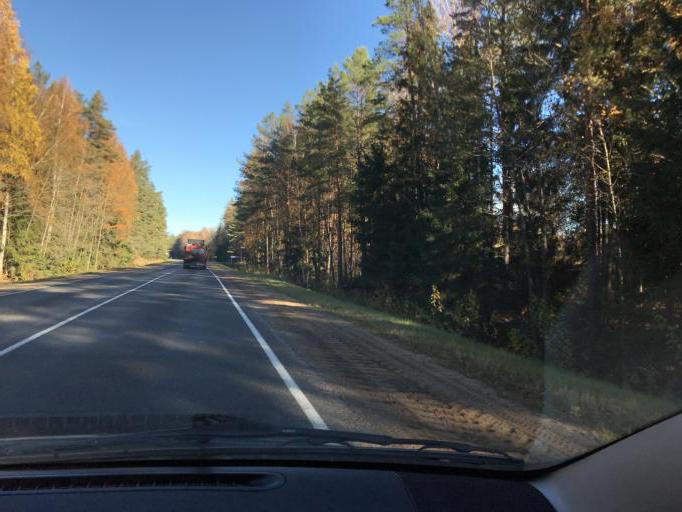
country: BY
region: Vitebsk
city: Polatsk
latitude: 55.3558
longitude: 28.8038
